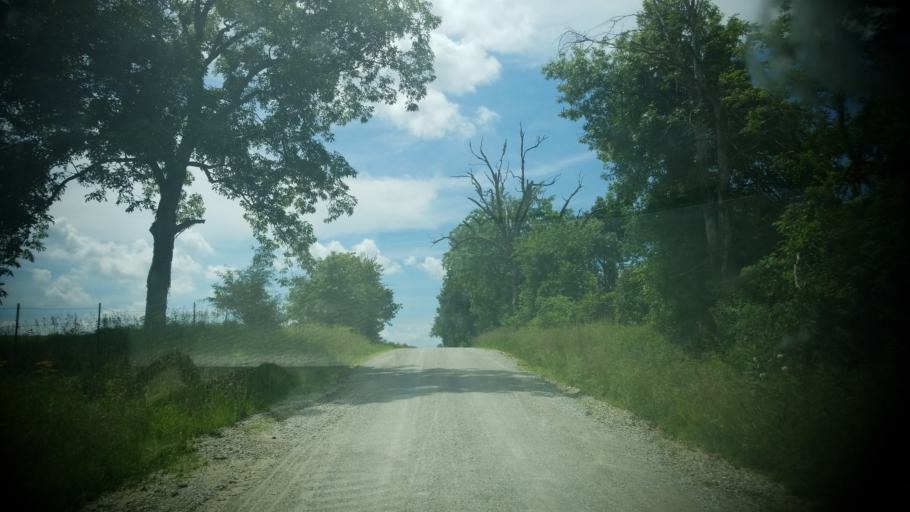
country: US
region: Missouri
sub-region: Pike County
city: Bowling Green
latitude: 39.3089
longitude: -91.3318
